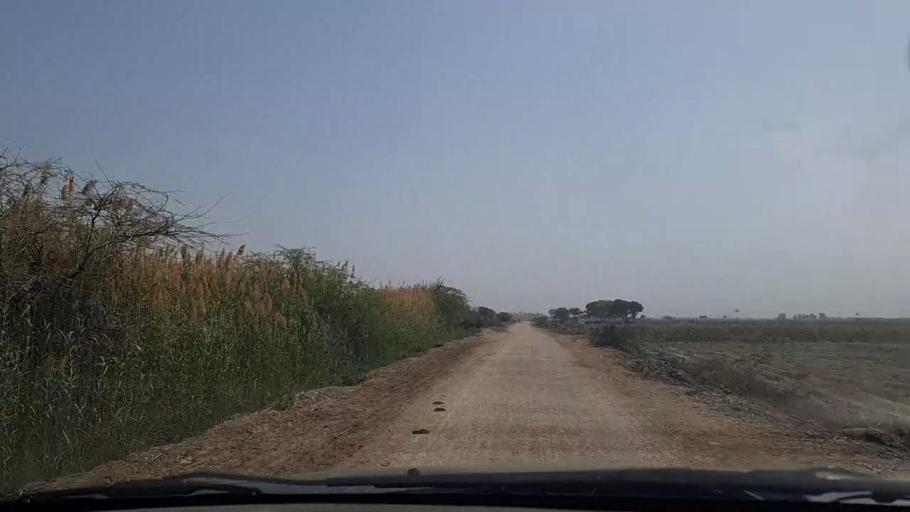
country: PK
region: Sindh
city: Keti Bandar
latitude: 24.2720
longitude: 67.6719
